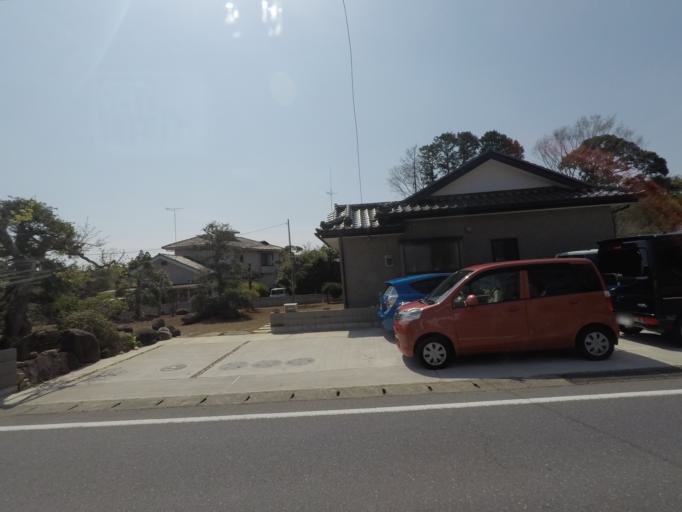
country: JP
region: Chiba
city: Narita
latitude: 35.7766
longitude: 140.3496
